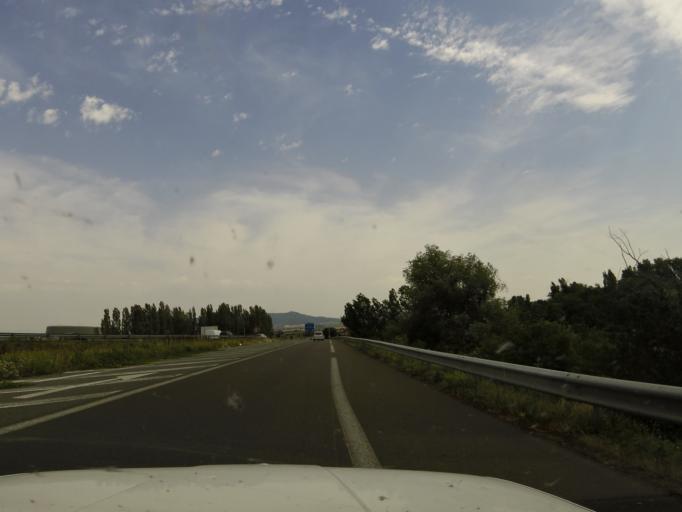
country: FR
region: Auvergne
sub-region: Departement du Puy-de-Dome
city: Perignat-les-Sarlieve
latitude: 45.7412
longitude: 3.1458
